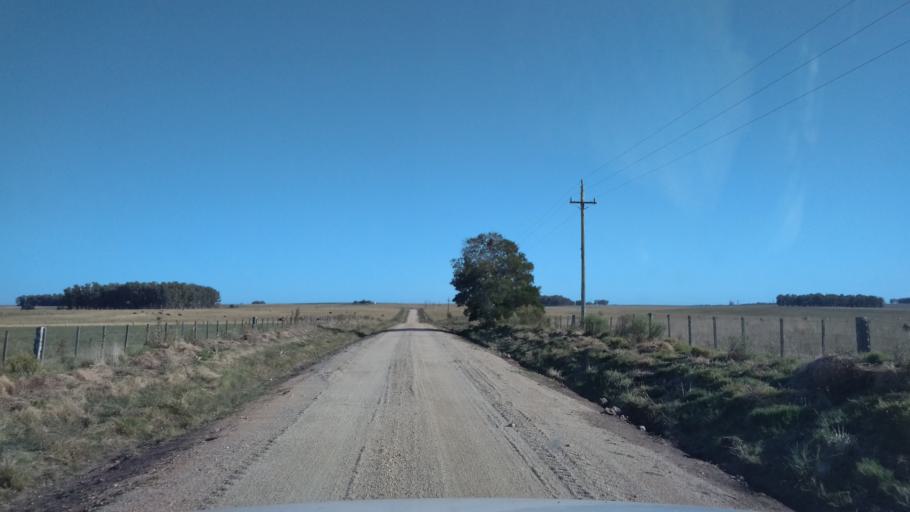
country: UY
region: Florida
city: Casupa
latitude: -34.0300
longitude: -55.7811
